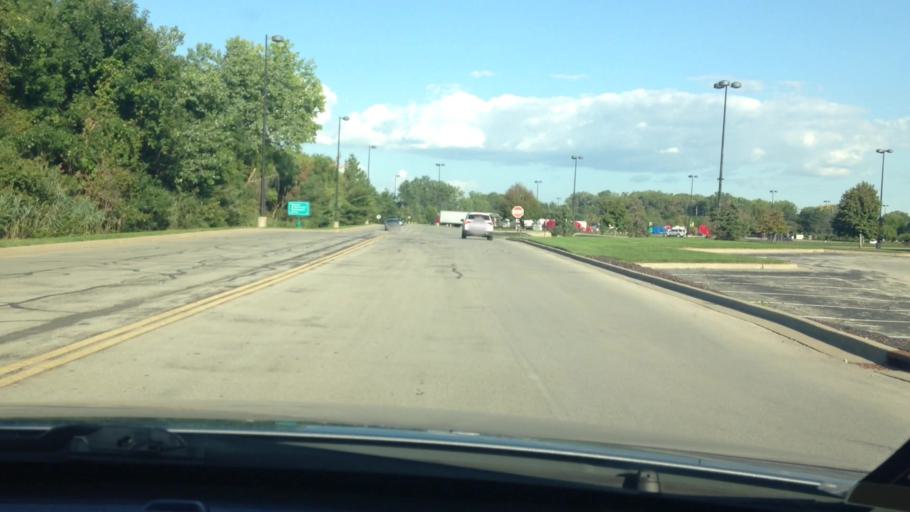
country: US
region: Missouri
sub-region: Clay County
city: Claycomo
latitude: 39.1535
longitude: -94.4852
